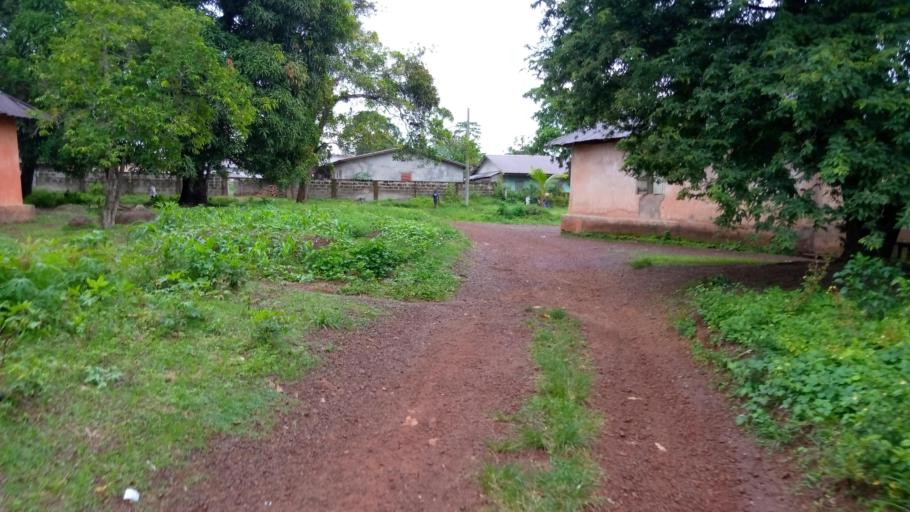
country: SL
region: Southern Province
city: Moyamba
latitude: 8.1634
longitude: -12.4380
